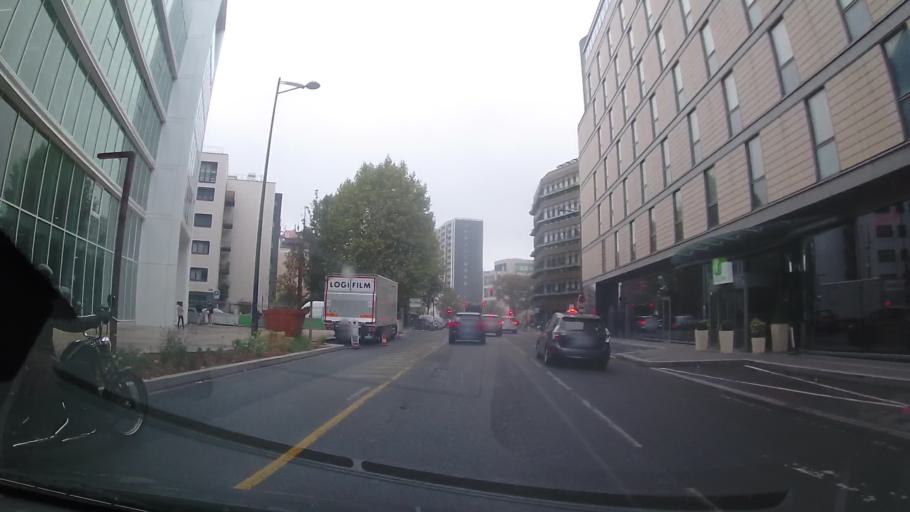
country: FR
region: Ile-de-France
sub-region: Departement des Hauts-de-Seine
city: Clichy
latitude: 48.8979
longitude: 2.3103
